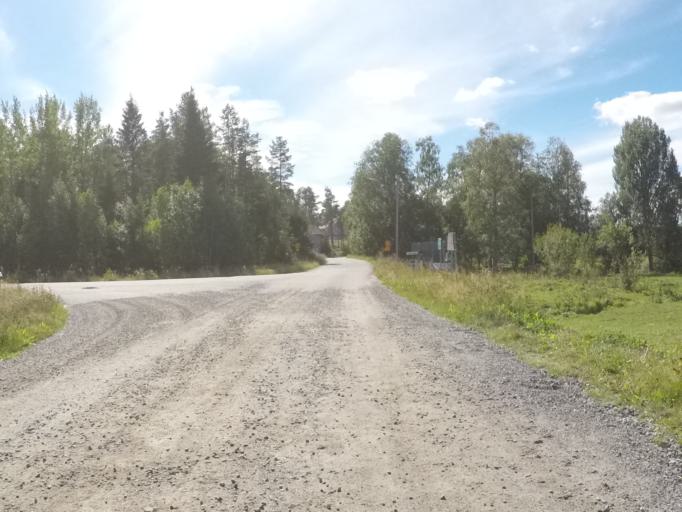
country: SE
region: Vaesterbotten
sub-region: Robertsfors Kommun
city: Robertsfors
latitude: 63.9992
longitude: 20.8103
